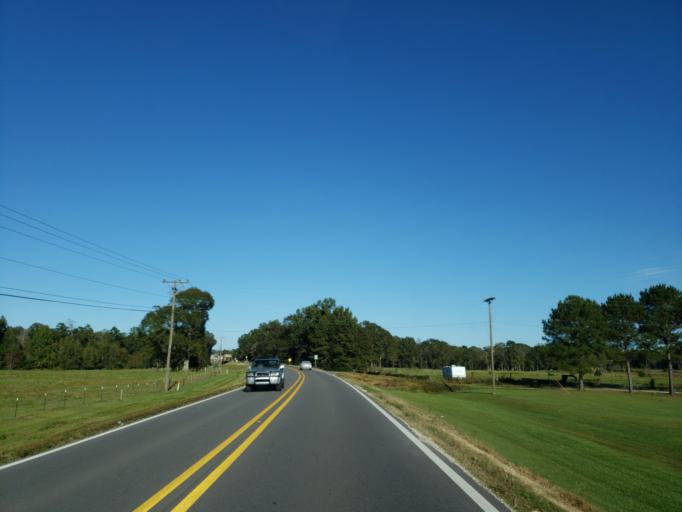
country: US
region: Mississippi
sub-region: Forrest County
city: Petal
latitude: 31.3706
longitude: -89.1258
